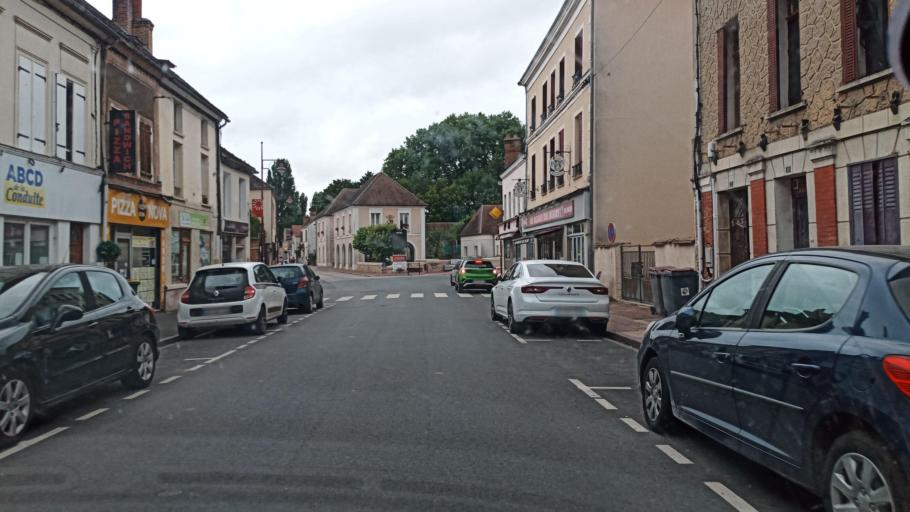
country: FR
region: Ile-de-France
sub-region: Departement de Seine-et-Marne
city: Voulx
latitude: 48.2814
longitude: 2.9693
